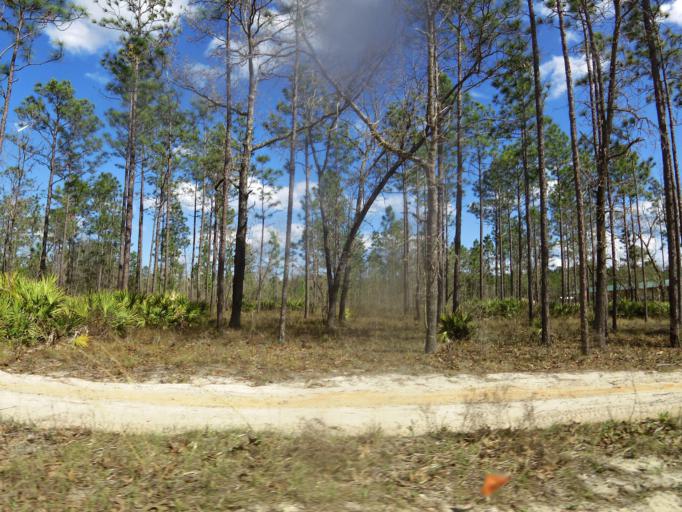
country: US
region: Florida
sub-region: Clay County
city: Middleburg
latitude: 30.1300
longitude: -81.9657
